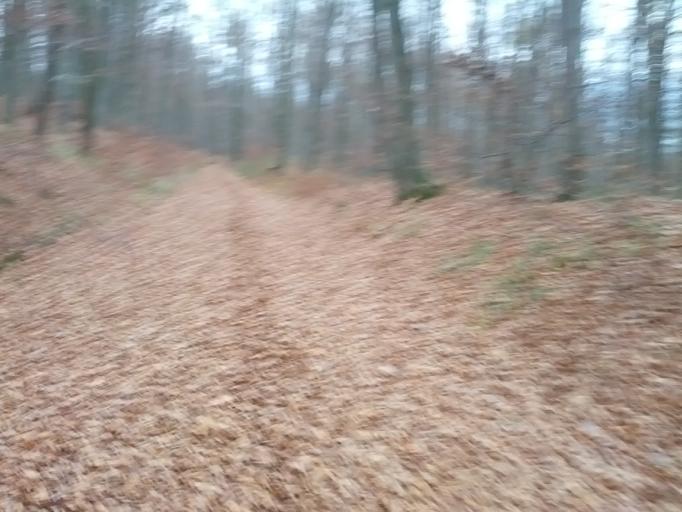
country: DE
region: Thuringia
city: Eisenach
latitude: 50.9382
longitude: 10.3194
